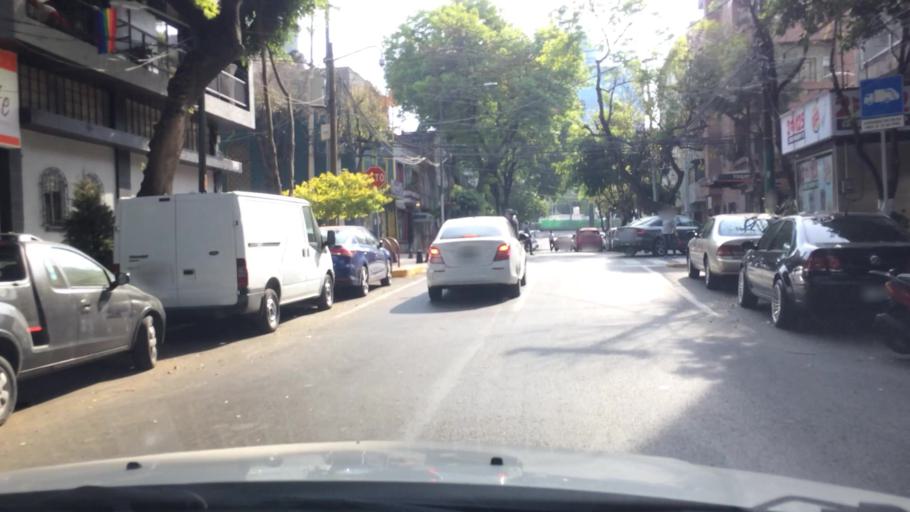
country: MX
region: Mexico City
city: Benito Juarez
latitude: 19.4007
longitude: -99.1717
